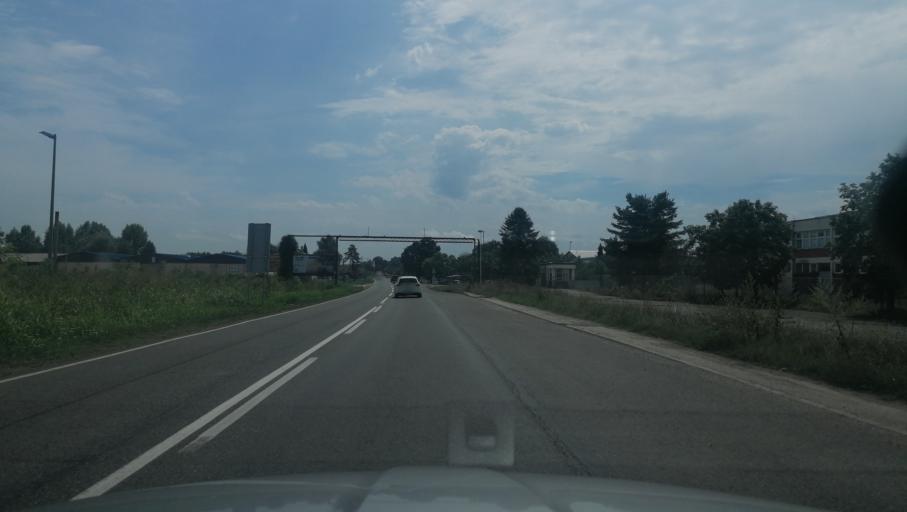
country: BA
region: Republika Srpska
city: Bosanski Samac
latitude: 45.0520
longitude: 18.4769
